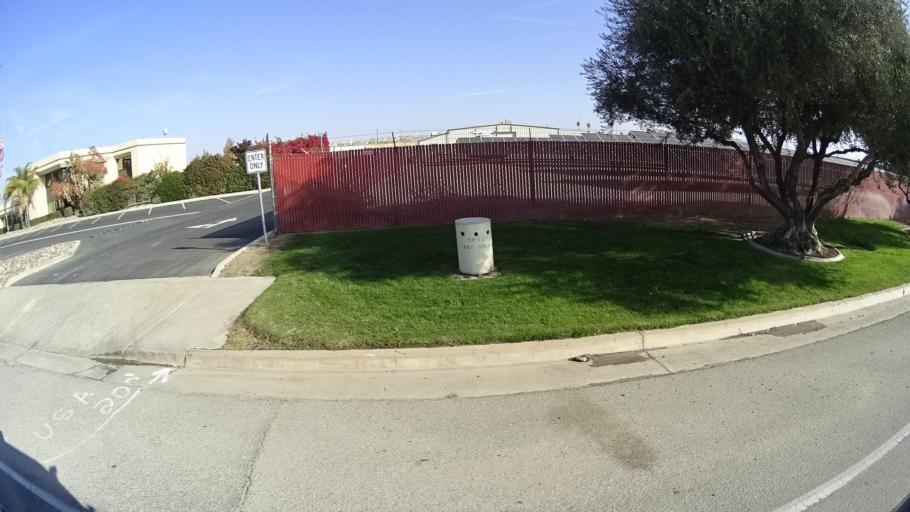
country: US
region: California
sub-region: Kern County
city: Oildale
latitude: 35.4534
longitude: -119.0387
